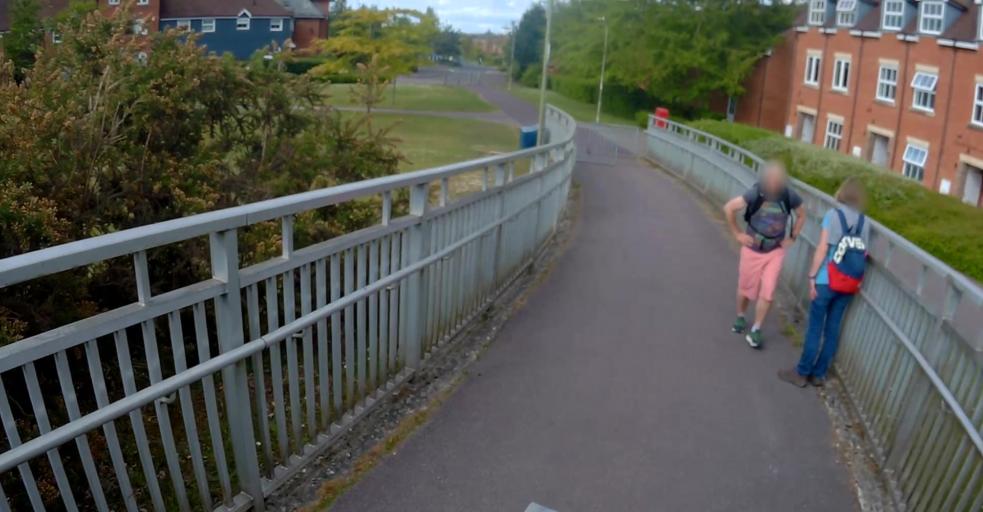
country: GB
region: England
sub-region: Hampshire
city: Fleet
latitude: 51.2901
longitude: -0.8479
